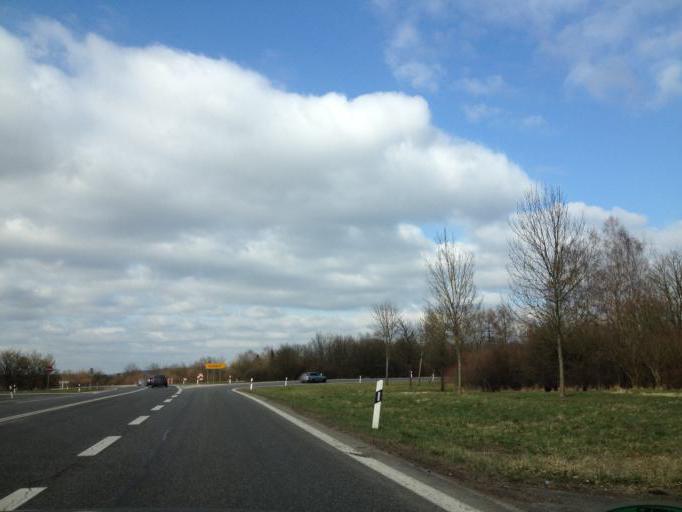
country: DE
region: Saarland
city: Sankt Wendel
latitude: 49.4693
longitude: 7.1492
